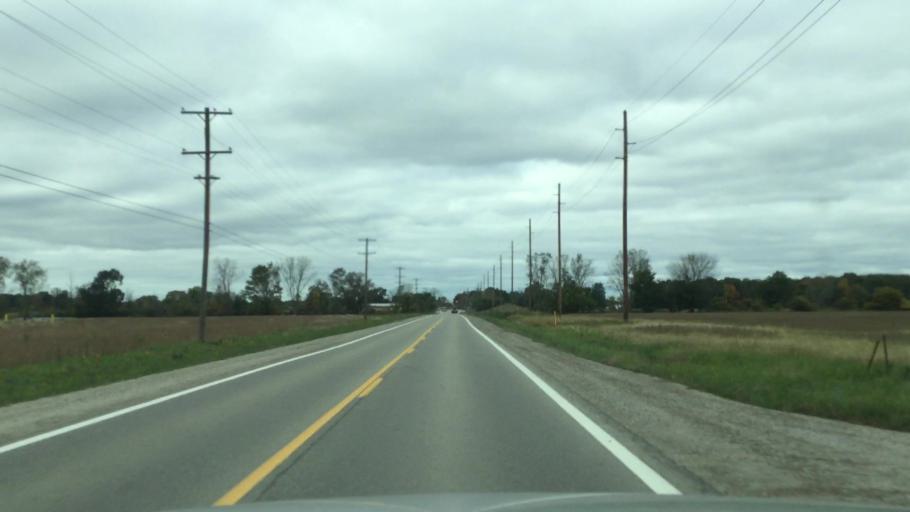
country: US
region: Michigan
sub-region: Macomb County
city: Armada
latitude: 42.8065
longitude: -82.8755
